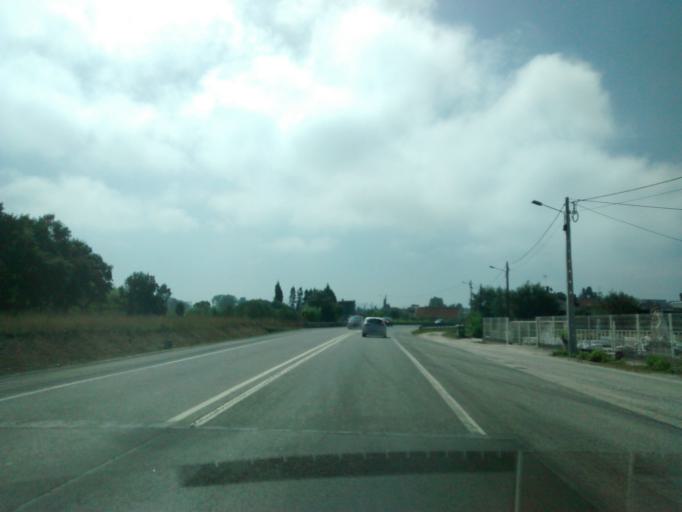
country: PT
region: Aveiro
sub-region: Mealhada
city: Mealhada
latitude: 40.3597
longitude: -8.4518
